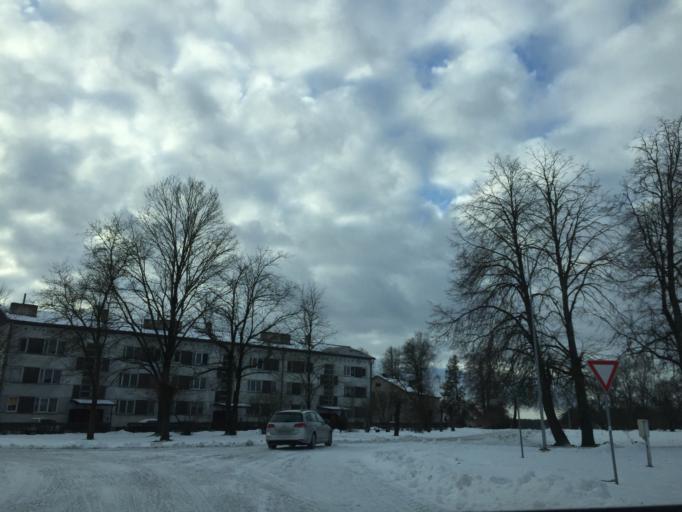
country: LV
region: Lielvarde
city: Lielvarde
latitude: 56.6315
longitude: 24.7528
